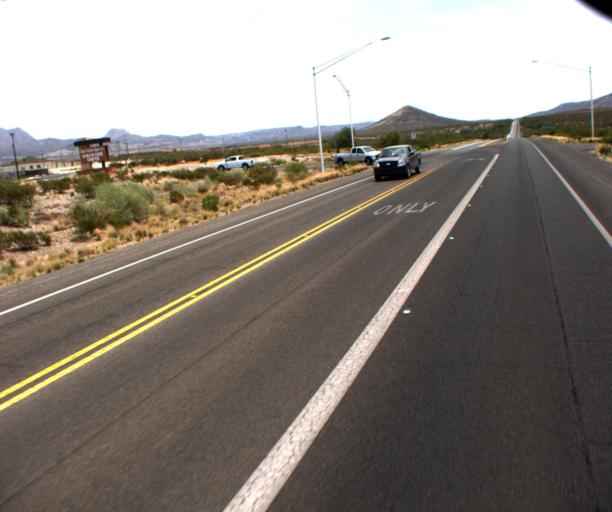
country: US
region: Arizona
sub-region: Gila County
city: Peridot
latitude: 33.2918
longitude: -110.4274
